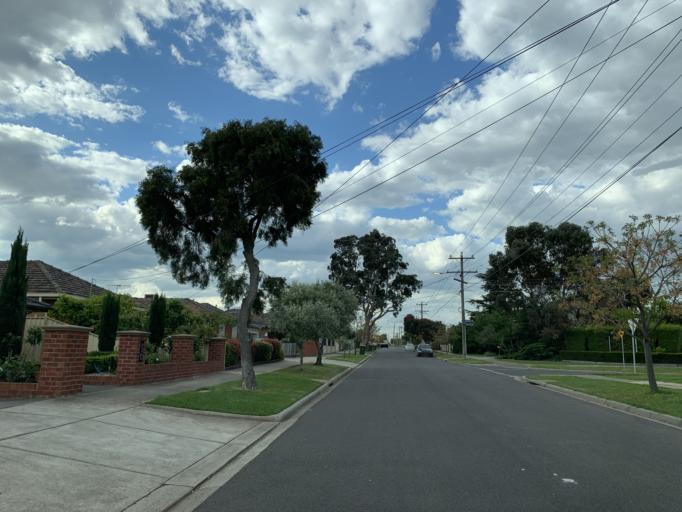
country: AU
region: Victoria
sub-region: Moonee Valley
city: Keilor East
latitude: -37.7520
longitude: 144.8530
